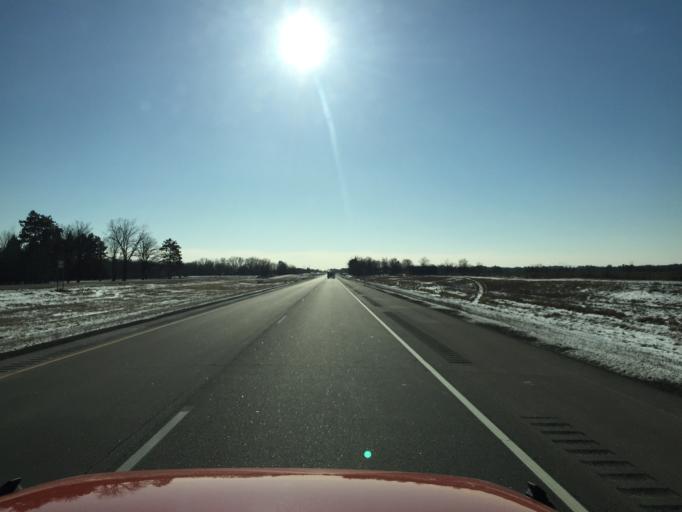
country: US
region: Minnesota
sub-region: Mille Lacs County
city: Milaca
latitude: 45.8070
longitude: -93.6551
